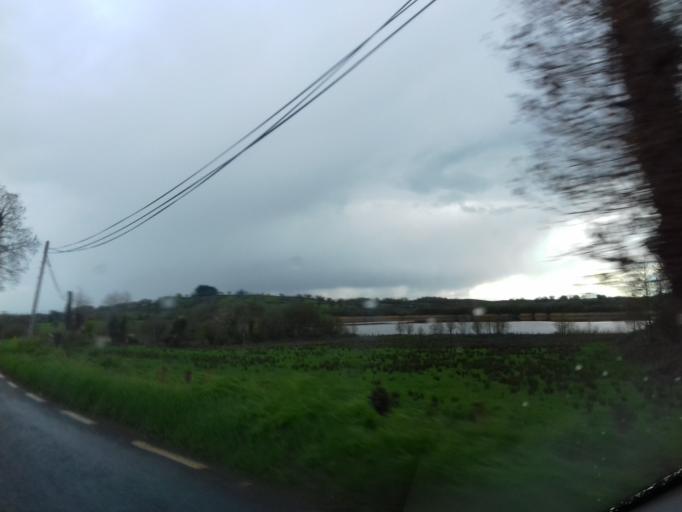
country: IE
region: Ulster
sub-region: An Cabhan
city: Ballyconnell
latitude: 54.1322
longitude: -7.6895
